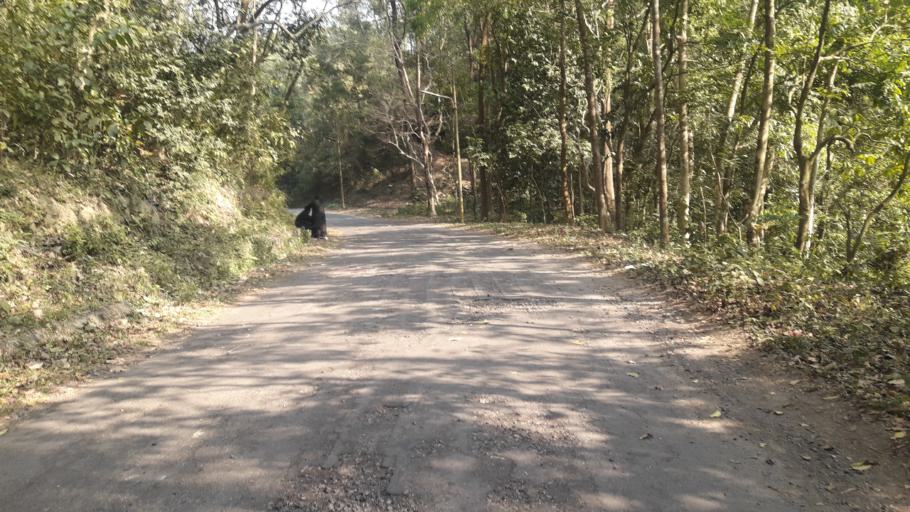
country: BD
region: Chittagong
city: Chittagong
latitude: 22.4664
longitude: 91.7900
